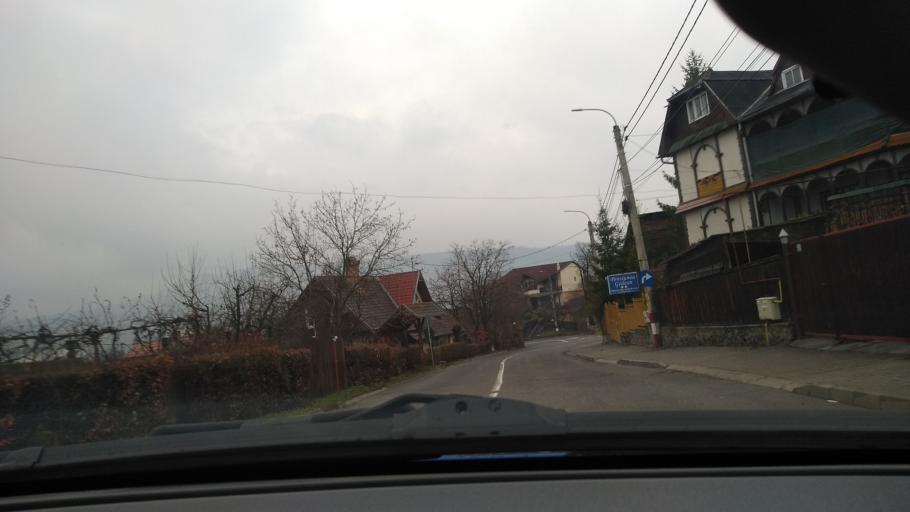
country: RO
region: Mures
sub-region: Oras Sovata
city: Sovata
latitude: 46.5966
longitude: 25.0753
